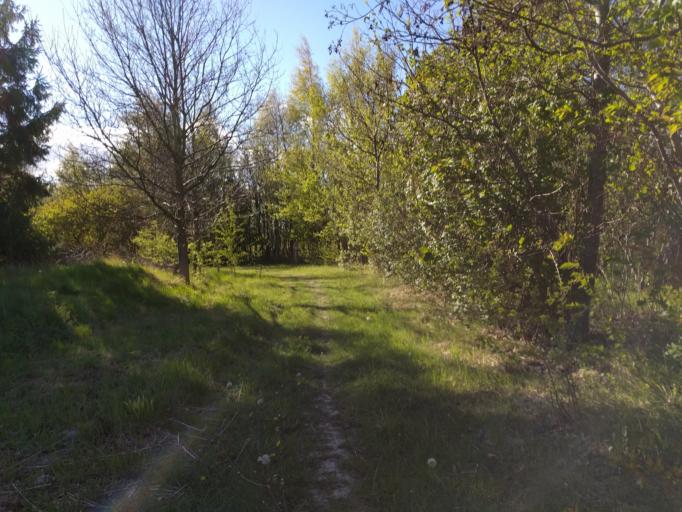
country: DK
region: South Denmark
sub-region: Kerteminde Kommune
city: Munkebo
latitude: 55.4571
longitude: 10.5224
